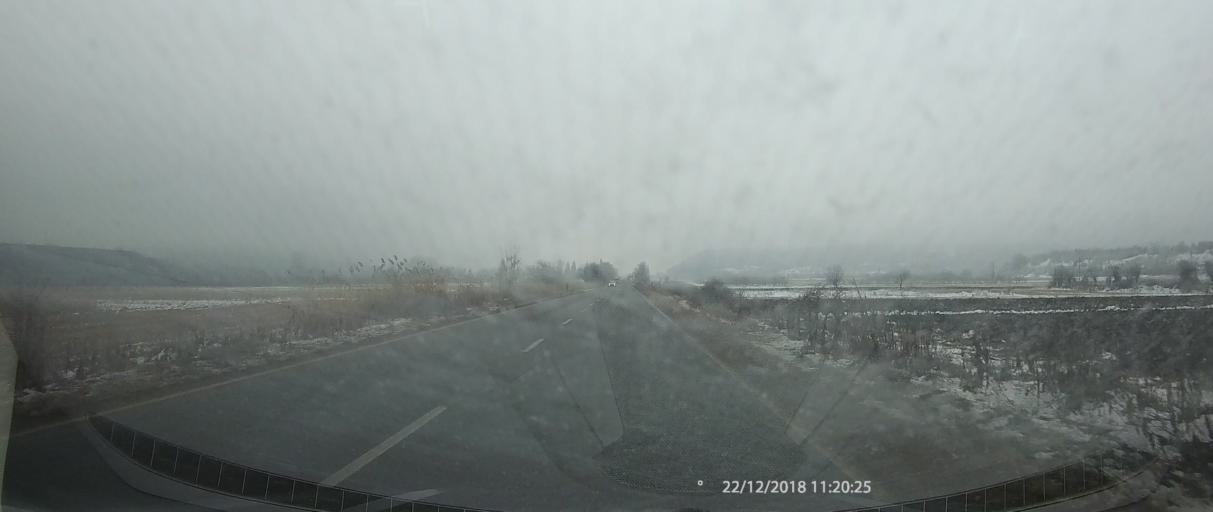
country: BG
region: Kyustendil
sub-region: Obshtina Kyustendil
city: Kyustendil
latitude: 42.2647
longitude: 22.8161
